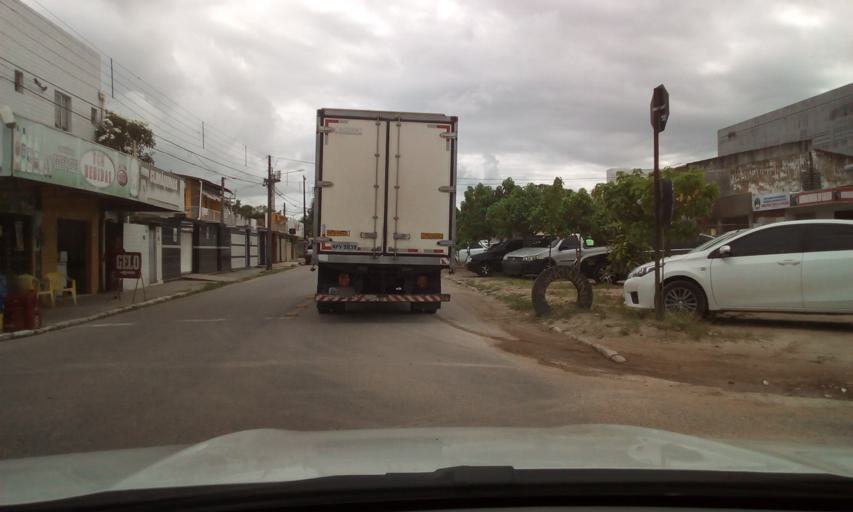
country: BR
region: Paraiba
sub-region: Joao Pessoa
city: Joao Pessoa
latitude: -7.1653
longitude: -34.8709
